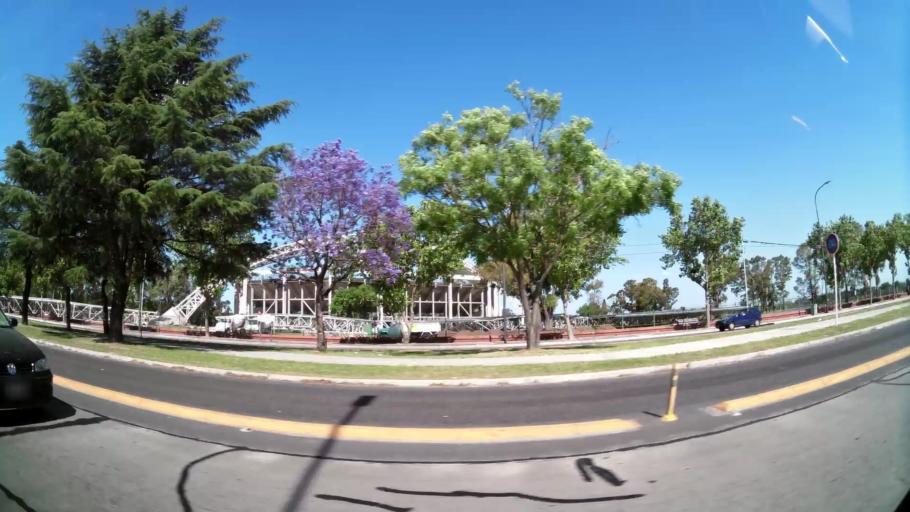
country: AR
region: Buenos Aires F.D.
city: Villa Lugano
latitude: -34.6771
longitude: -58.4488
